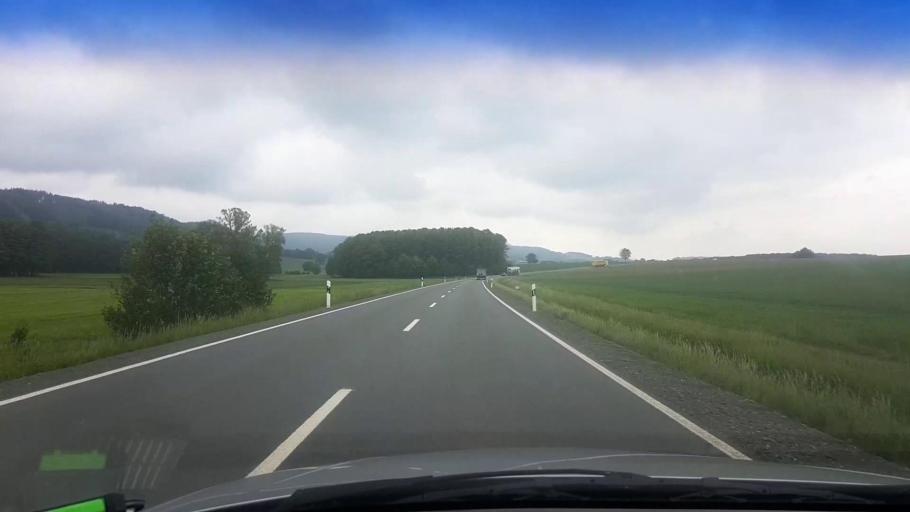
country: DE
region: Bavaria
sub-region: Upper Franconia
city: Gesees
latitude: 50.0251
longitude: 11.6612
